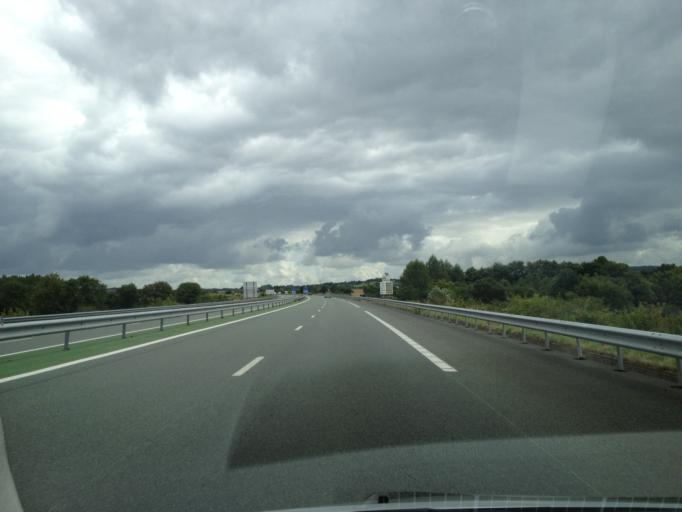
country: FR
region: Pays de la Loire
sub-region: Departement de la Vendee
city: Beaurepaire
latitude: 46.8978
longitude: -1.0677
